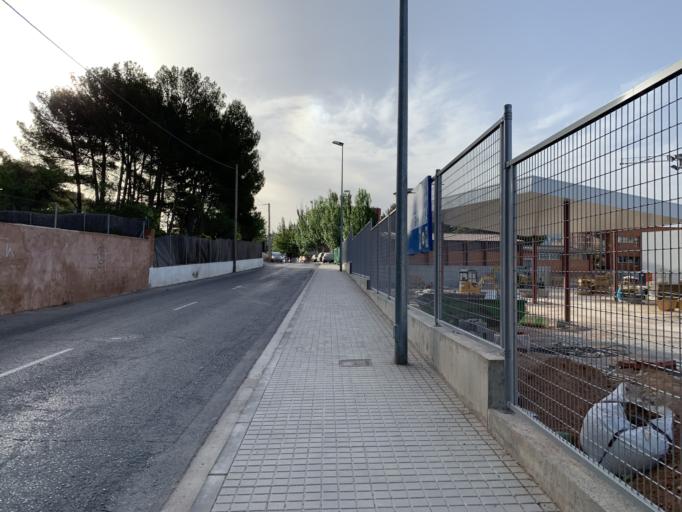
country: ES
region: Aragon
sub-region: Provincia de Teruel
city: Teruel
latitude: 40.3537
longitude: -1.1124
